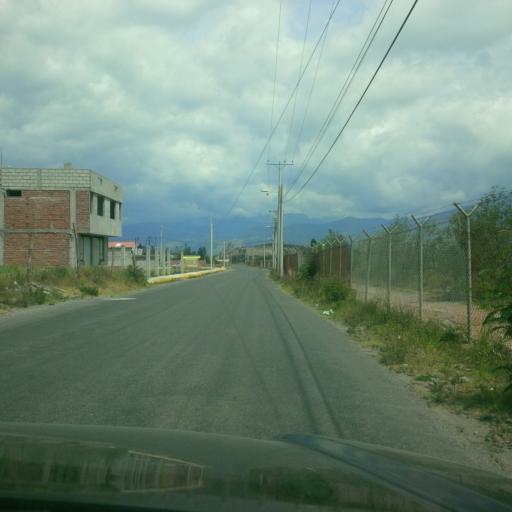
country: EC
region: Chimborazo
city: Riobamba
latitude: -1.6428
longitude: -78.6597
